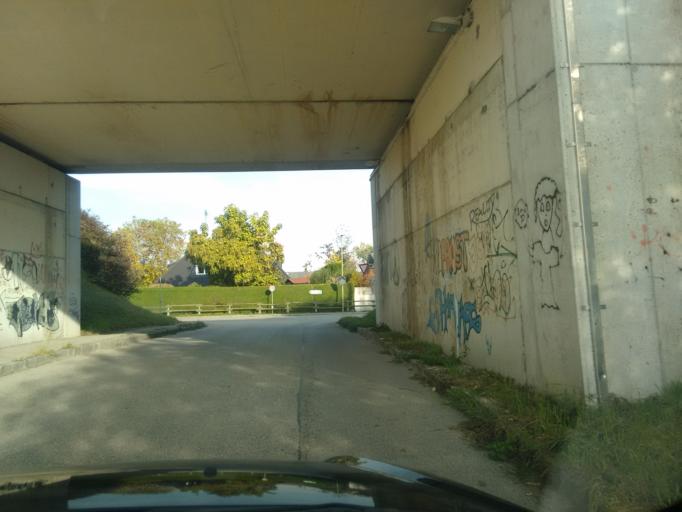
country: AT
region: Upper Austria
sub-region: Wels Stadt
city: Wels
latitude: 48.1866
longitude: 14.0011
